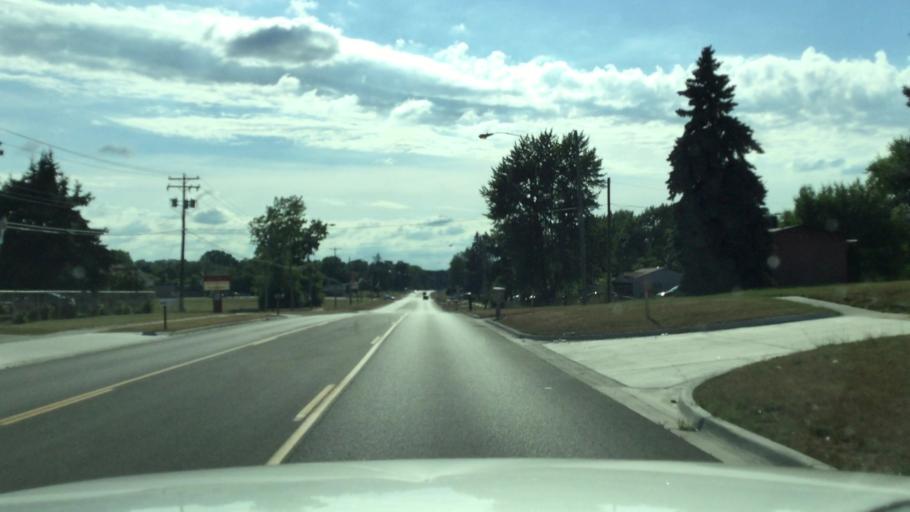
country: US
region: Michigan
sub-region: Genesee County
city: Beecher
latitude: 43.0901
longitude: -83.7168
